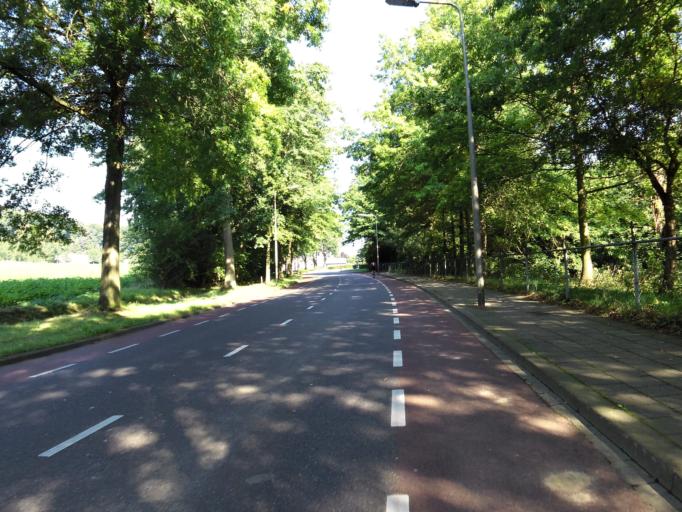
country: DE
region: North Rhine-Westphalia
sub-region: Regierungsbezirk Koln
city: Herzogenrath
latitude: 50.8754
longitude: 6.0859
